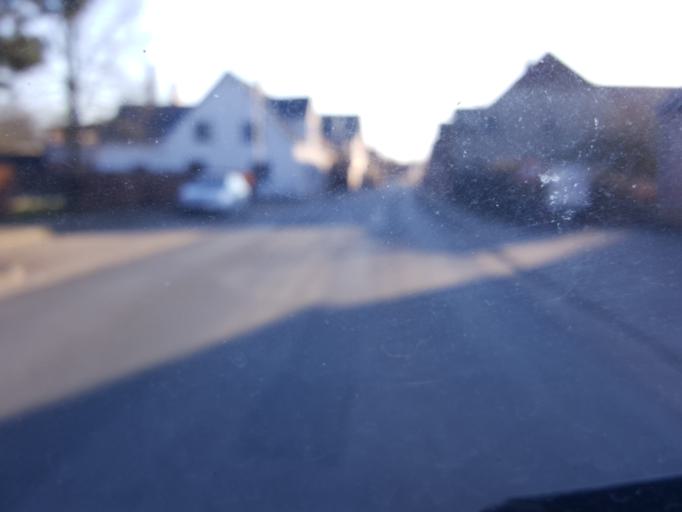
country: DE
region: North Rhine-Westphalia
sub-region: Regierungsbezirk Detmold
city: Hille
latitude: 52.4218
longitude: 8.7241
